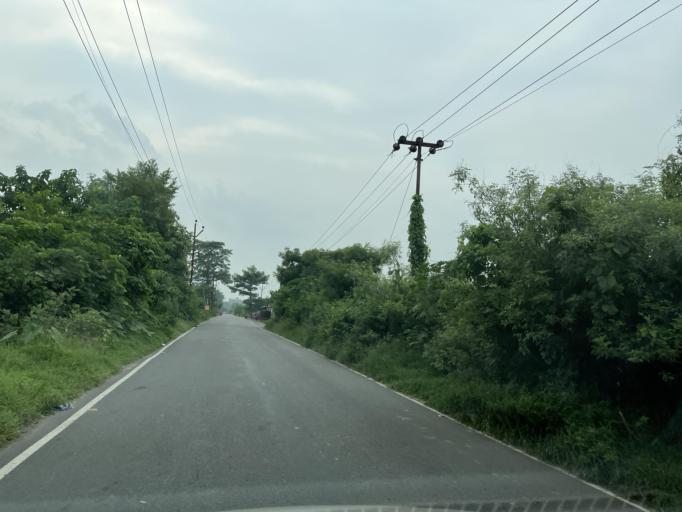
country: IN
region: Uttarakhand
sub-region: Naini Tal
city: Haldwani
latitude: 29.1739
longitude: 79.4737
